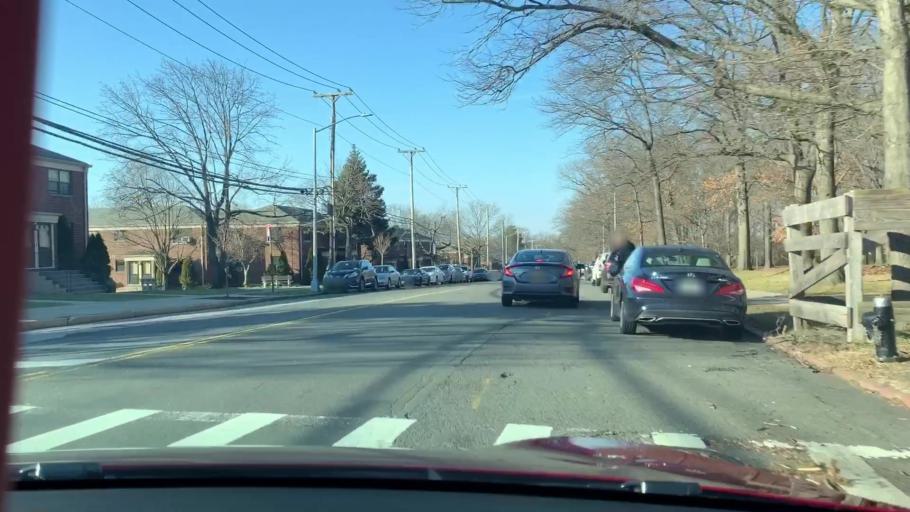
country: US
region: New York
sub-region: Nassau County
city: Bellerose Terrace
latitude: 40.7403
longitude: -73.7515
